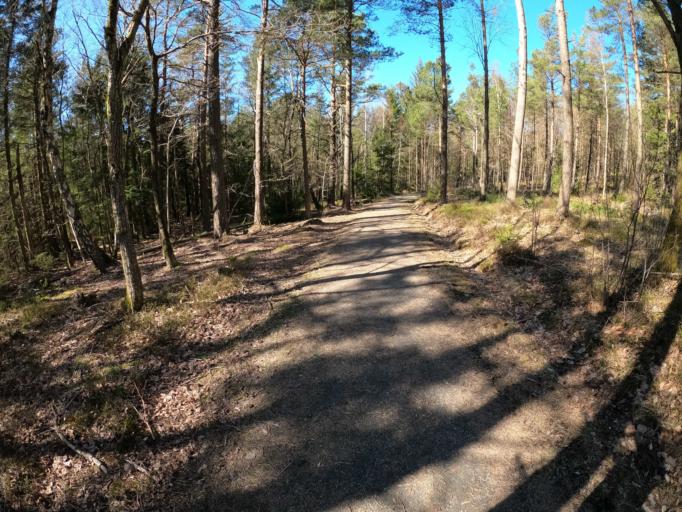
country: SE
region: Vaestra Goetaland
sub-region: Harryda Kommun
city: Molnlycke
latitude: 57.6197
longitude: 12.1099
